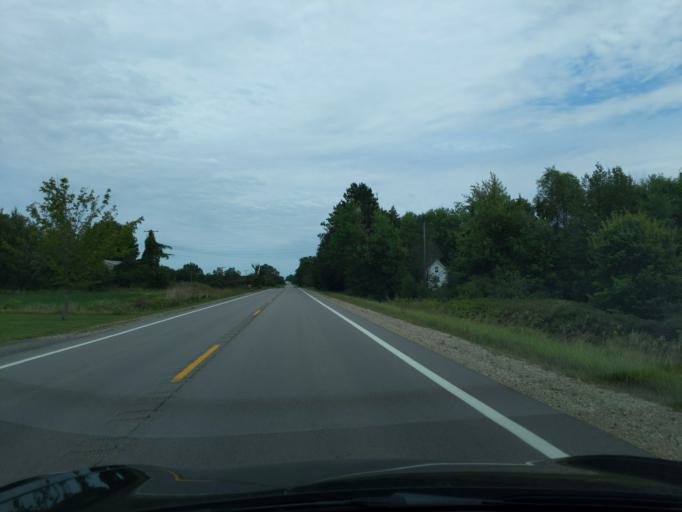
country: US
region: Michigan
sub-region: Barry County
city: Nashville
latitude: 42.5673
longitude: -85.0615
